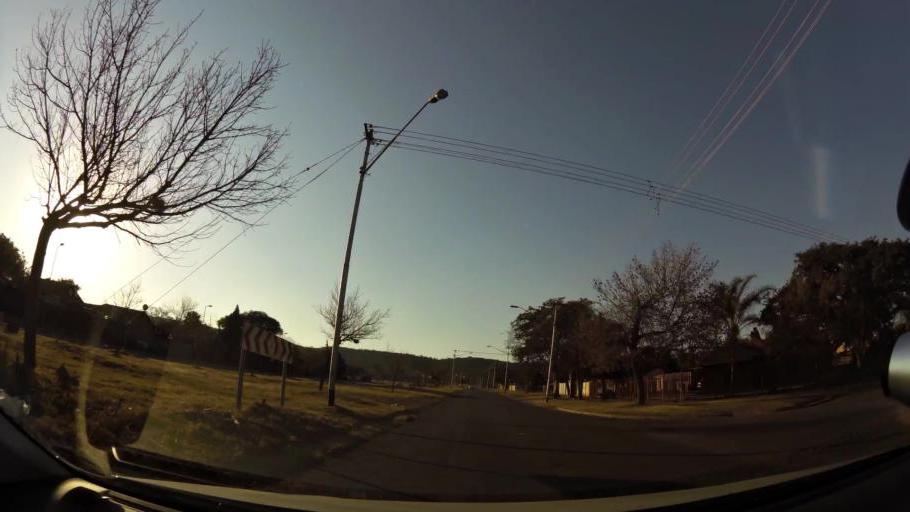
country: ZA
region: Gauteng
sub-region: City of Tshwane Metropolitan Municipality
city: Pretoria
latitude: -25.7401
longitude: 28.1174
